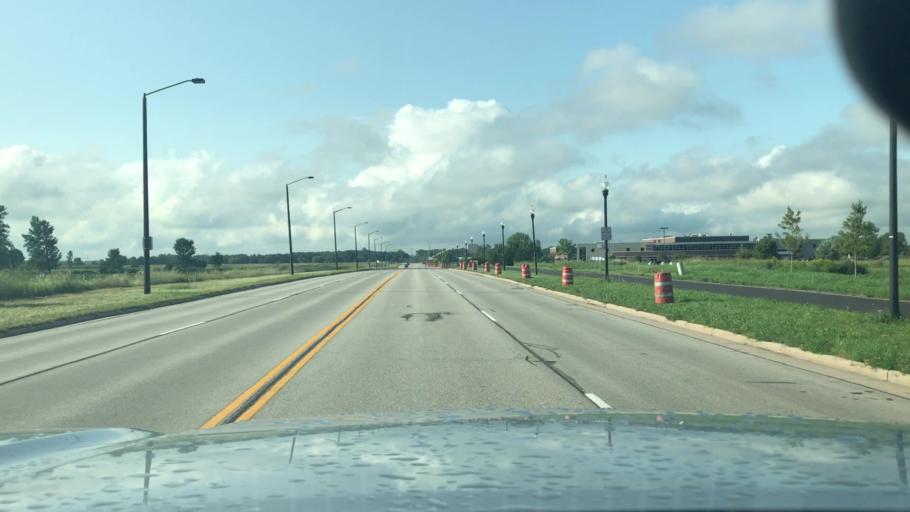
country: US
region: Wisconsin
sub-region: Brown County
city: Bellevue
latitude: 44.4717
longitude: -87.9171
